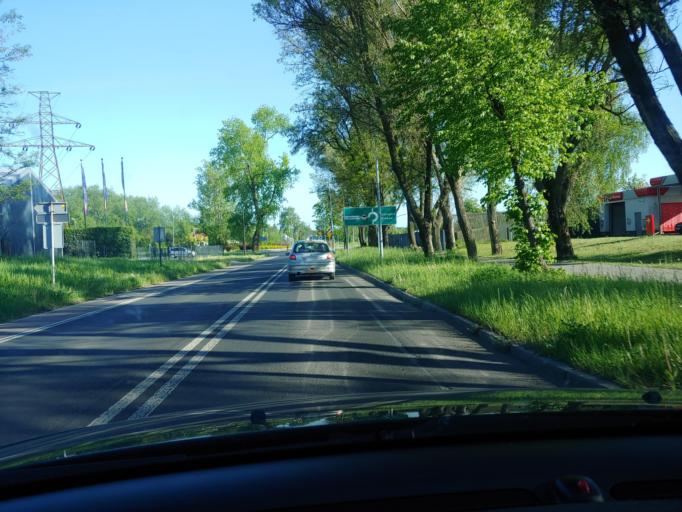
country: PL
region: Silesian Voivodeship
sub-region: Jaworzno
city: Jaworzno
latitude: 50.1906
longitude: 19.2855
